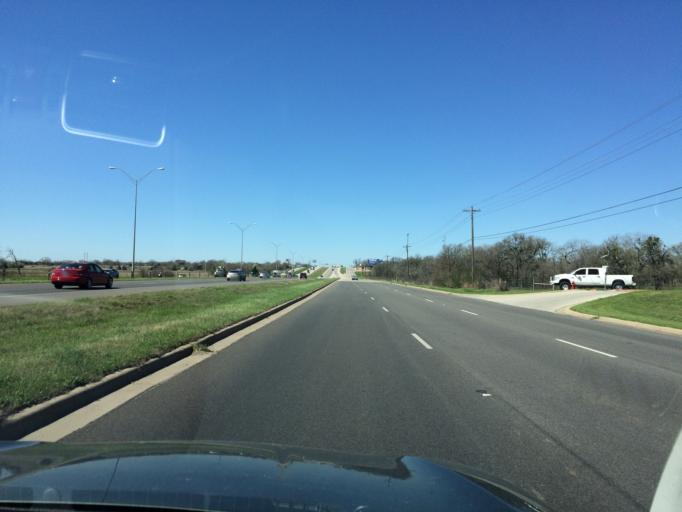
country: US
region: Texas
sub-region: Bastrop County
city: Bastrop
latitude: 30.1114
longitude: -97.3571
